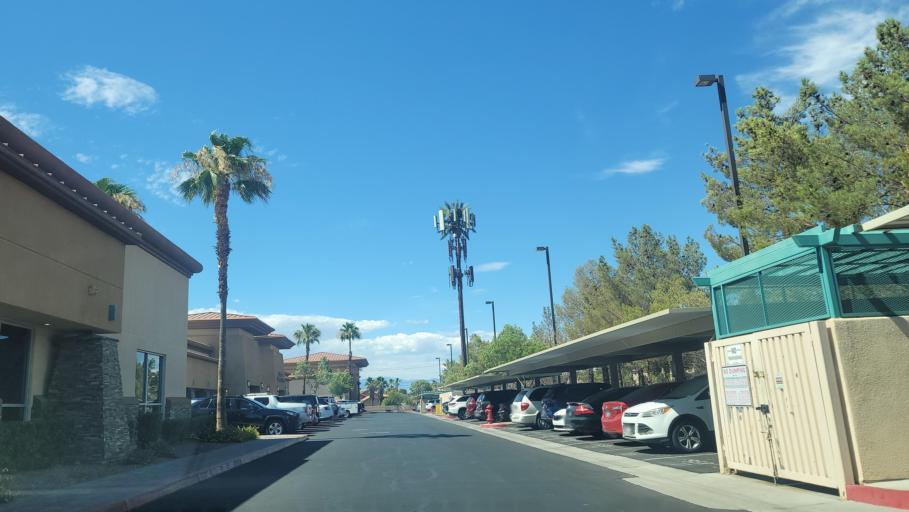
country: US
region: Nevada
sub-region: Clark County
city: Spring Valley
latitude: 36.0983
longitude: -115.2407
